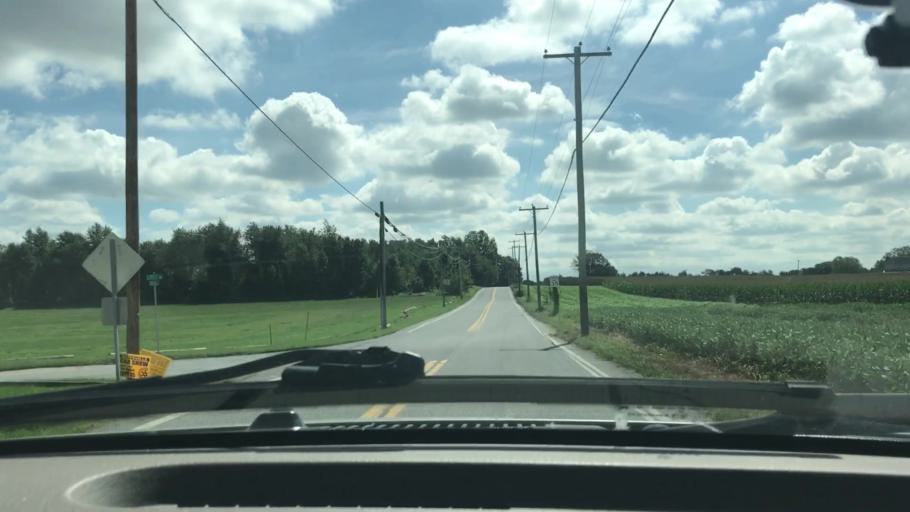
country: US
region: Pennsylvania
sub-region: Lancaster County
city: East Petersburg
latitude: 40.1165
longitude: -76.3795
